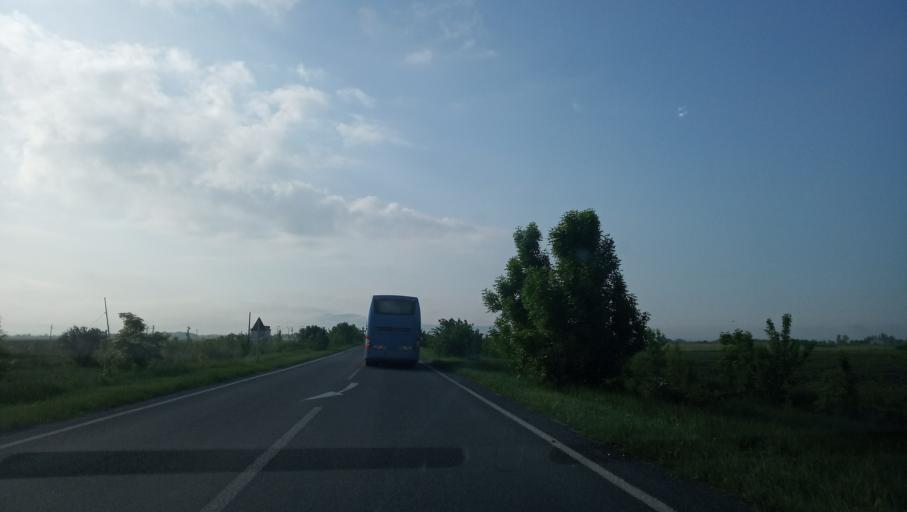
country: RO
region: Timis
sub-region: Comuna Moravita
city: Moravita
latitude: 45.2427
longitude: 21.2633
